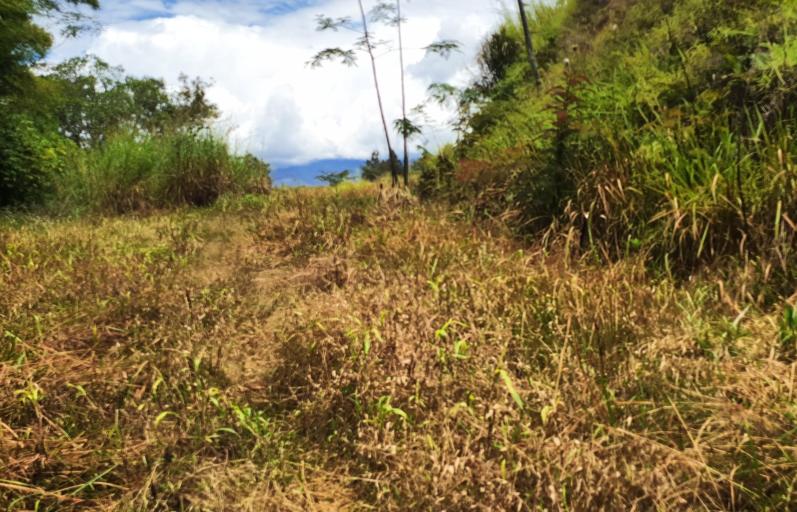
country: PG
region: Jiwaka
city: Minj
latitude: -5.9158
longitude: 144.8245
